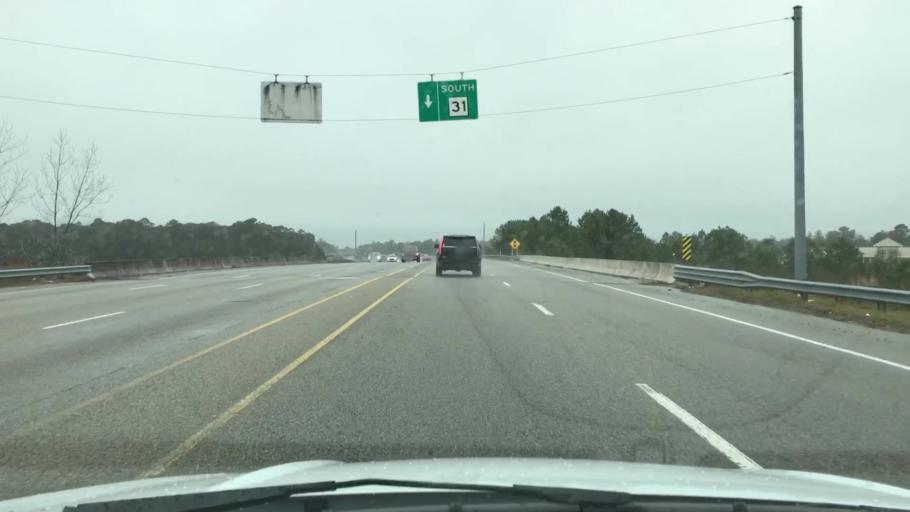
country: US
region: South Carolina
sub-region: Horry County
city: Myrtle Beach
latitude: 33.7536
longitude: -78.8522
